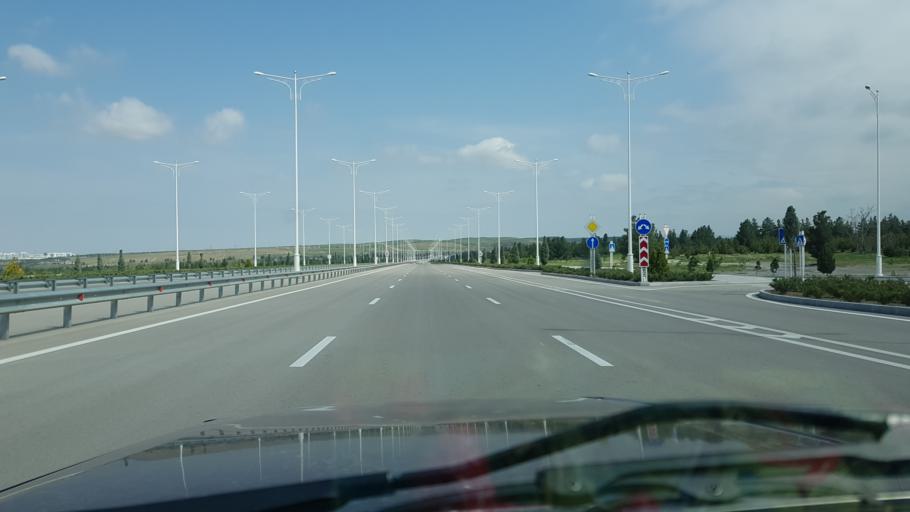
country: TM
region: Ahal
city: Ashgabat
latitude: 37.8641
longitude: 58.3581
